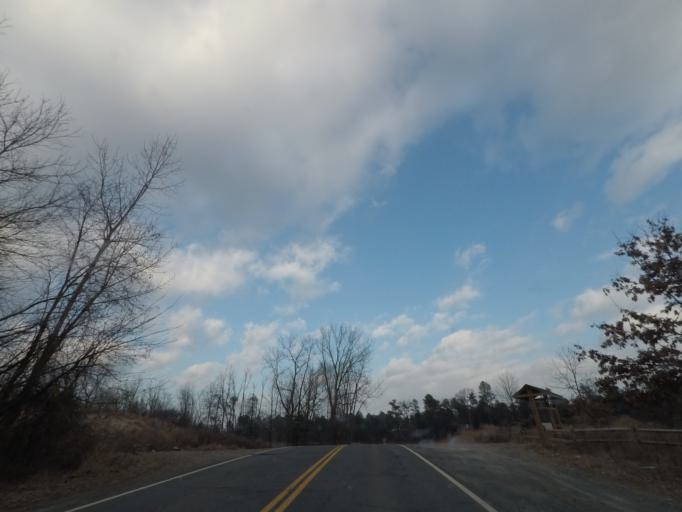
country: US
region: New York
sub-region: Albany County
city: Colonie
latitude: 42.7041
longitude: -73.8460
